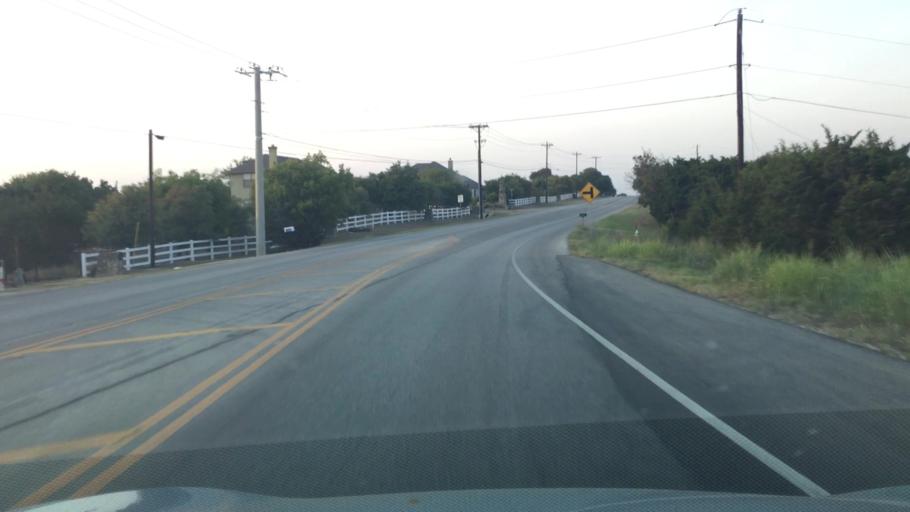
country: US
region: Texas
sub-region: Hays County
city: Dripping Springs
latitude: 30.1817
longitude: -98.0018
